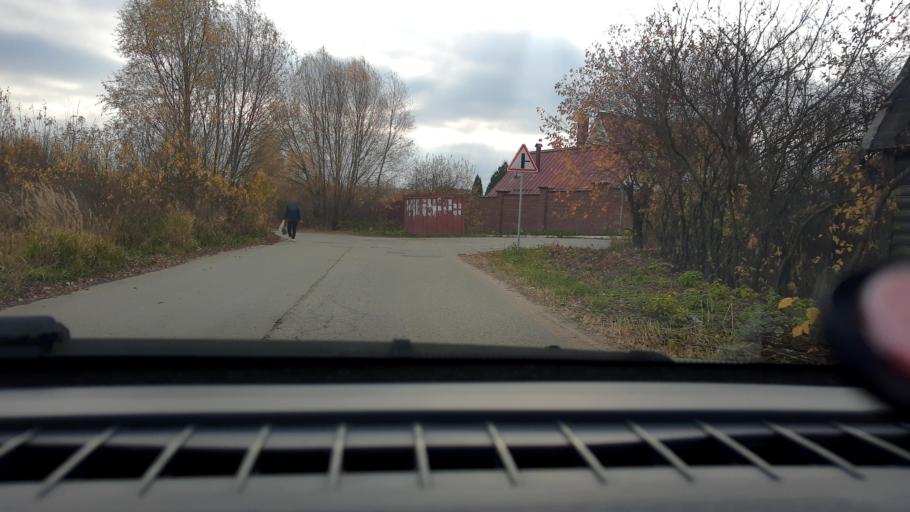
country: RU
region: Nizjnij Novgorod
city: Afonino
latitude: 56.2008
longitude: 44.0956
